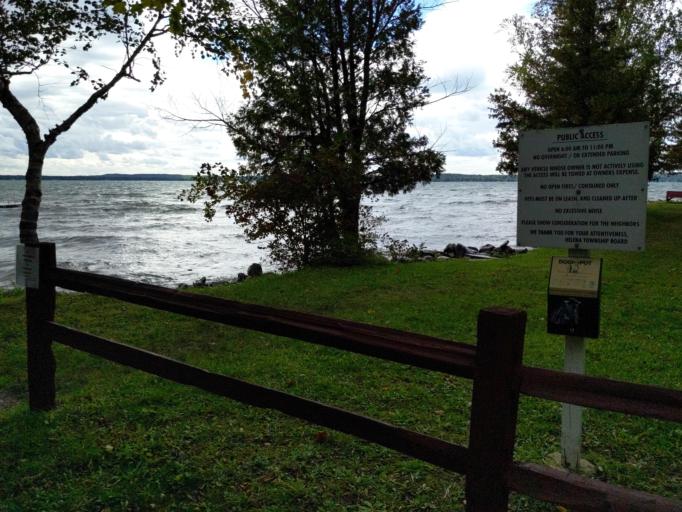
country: US
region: Michigan
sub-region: Kalkaska County
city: Rapid City
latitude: 44.8886
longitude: -85.2746
